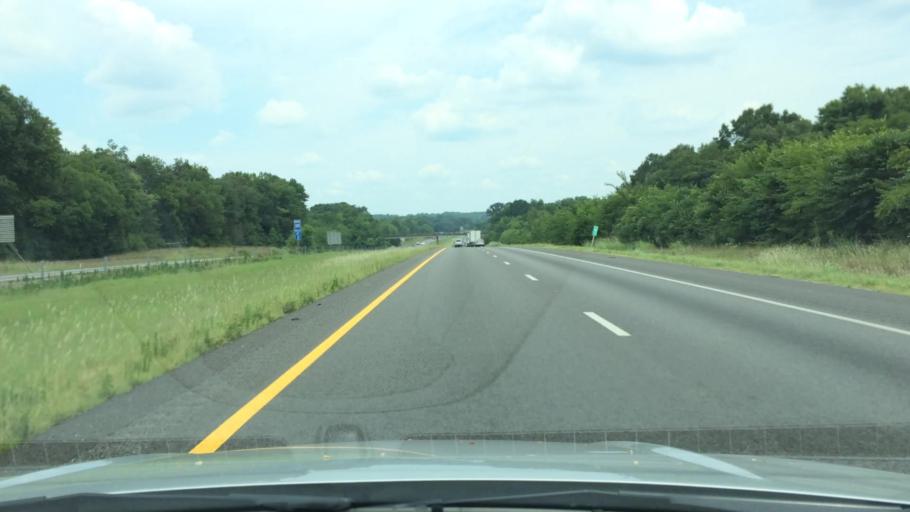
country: US
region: Tennessee
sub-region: Maury County
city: Spring Hill
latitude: 35.6567
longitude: -86.8926
